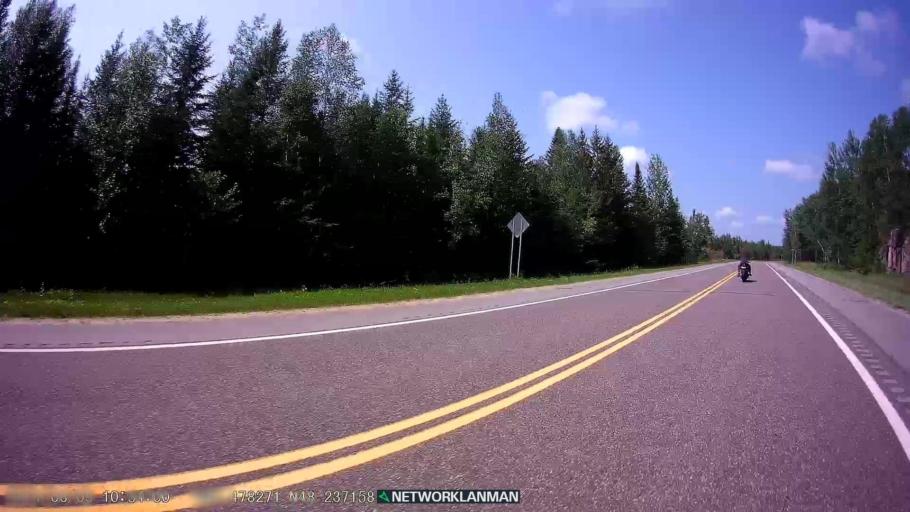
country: US
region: Minnesota
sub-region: Saint Louis County
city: Ely
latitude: 48.2374
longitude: -92.4786
